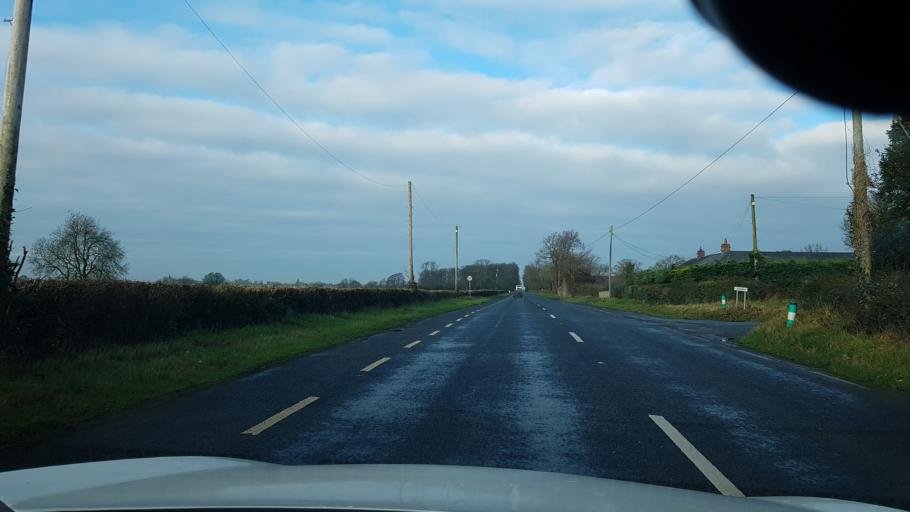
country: IE
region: Leinster
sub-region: An Mhi
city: Navan
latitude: 53.6174
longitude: -6.6401
